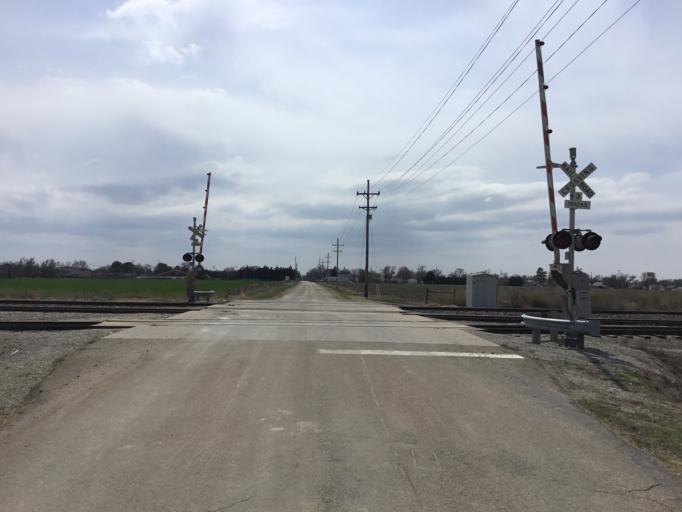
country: US
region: Kansas
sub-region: Russell County
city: Russell
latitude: 38.8965
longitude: -98.8451
